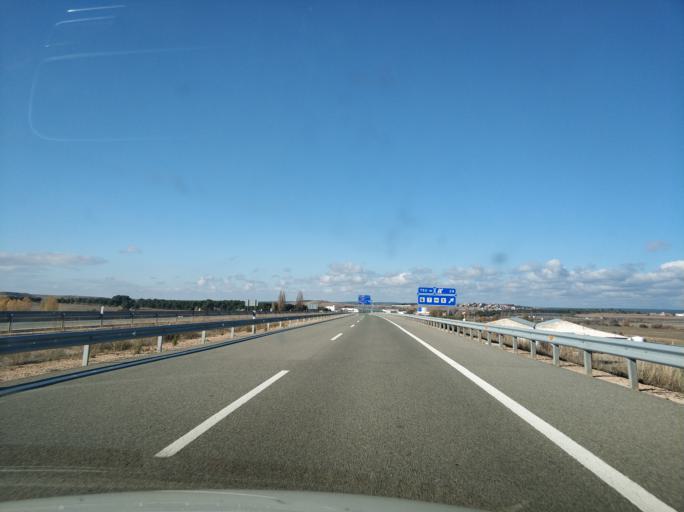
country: ES
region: Castille and Leon
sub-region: Provincia de Soria
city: Almazan
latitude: 41.4598
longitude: -2.5183
